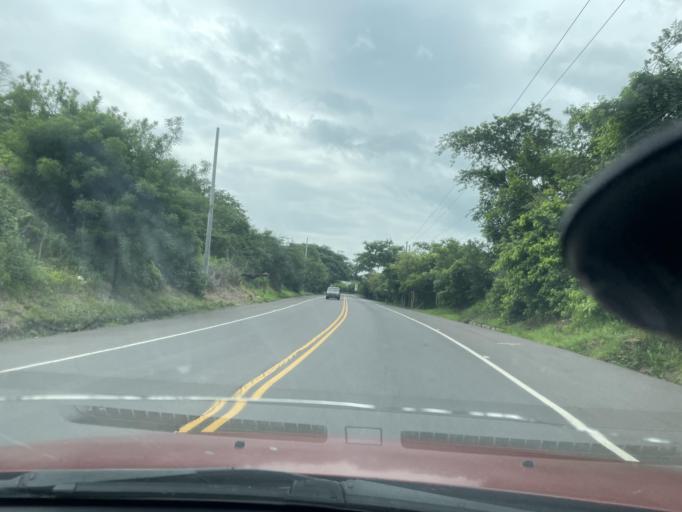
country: SV
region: San Miguel
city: Chirilagua
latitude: 13.3287
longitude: -88.1586
